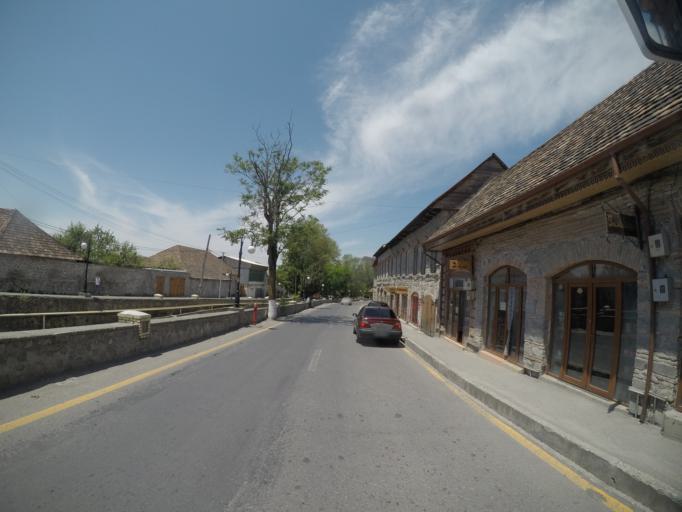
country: AZ
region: Shaki City
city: Sheki
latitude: 41.2014
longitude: 47.1831
